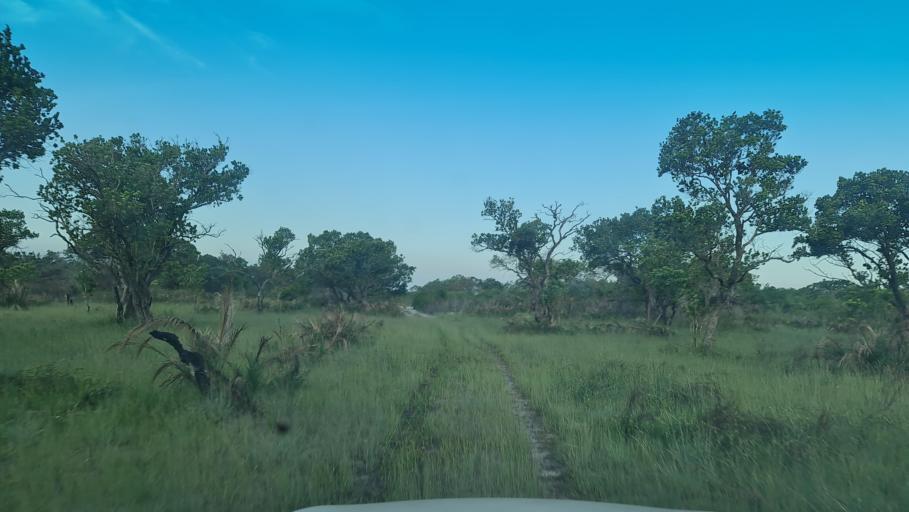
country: MZ
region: Gaza
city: Macia
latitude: -25.2152
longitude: 33.0515
